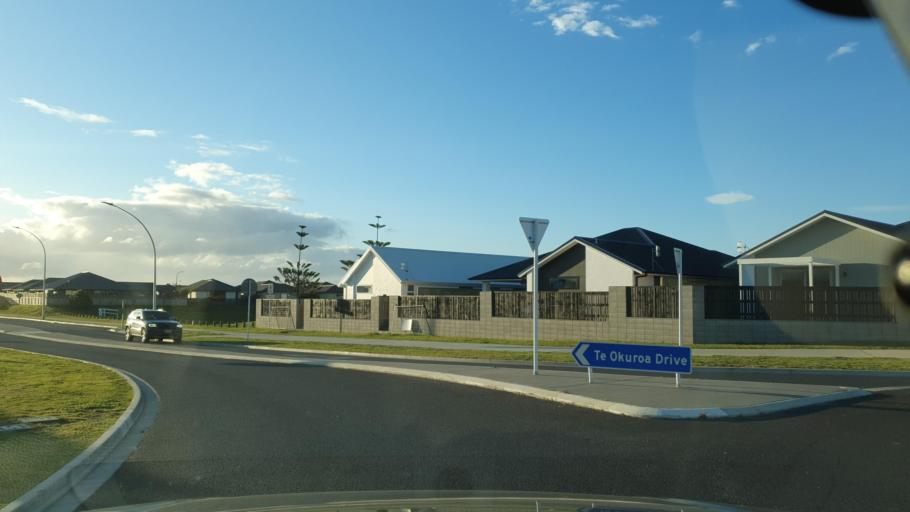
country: NZ
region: Bay of Plenty
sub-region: Western Bay of Plenty District
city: Maketu
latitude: -37.7274
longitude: 176.3368
